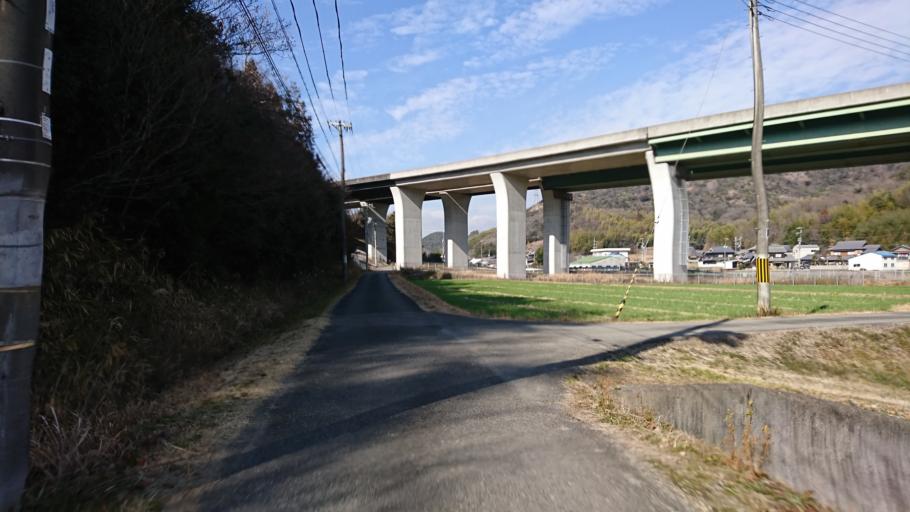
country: JP
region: Hyogo
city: Ono
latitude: 34.8385
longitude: 134.8638
